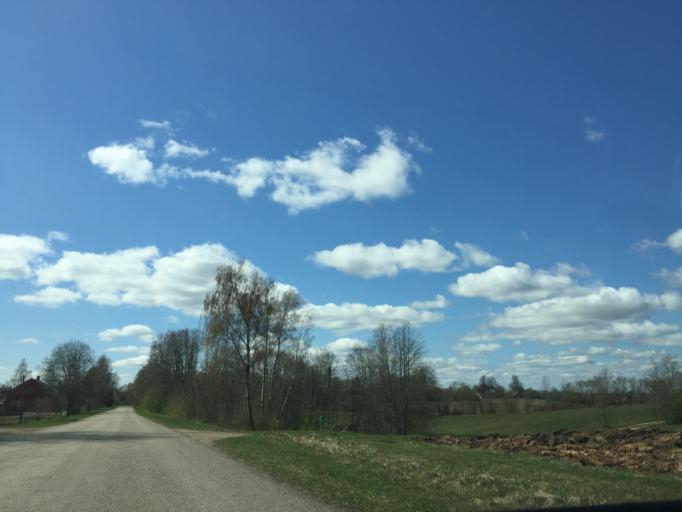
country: LV
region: Rezekne
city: Rezekne
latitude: 56.6460
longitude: 27.1789
